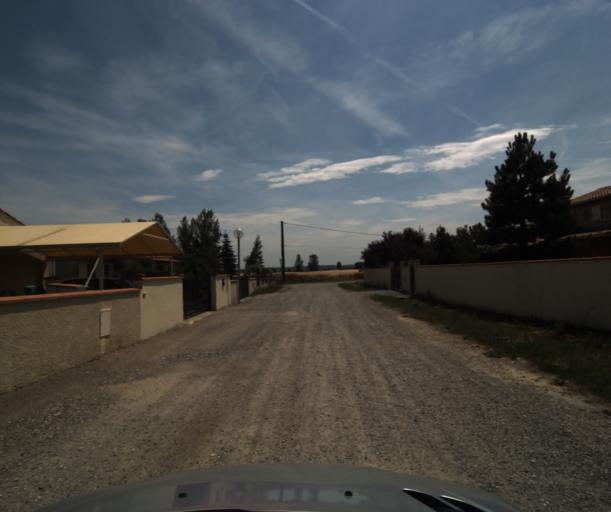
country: FR
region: Midi-Pyrenees
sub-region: Departement de la Haute-Garonne
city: Labastidette
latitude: 43.4566
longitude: 1.2468
